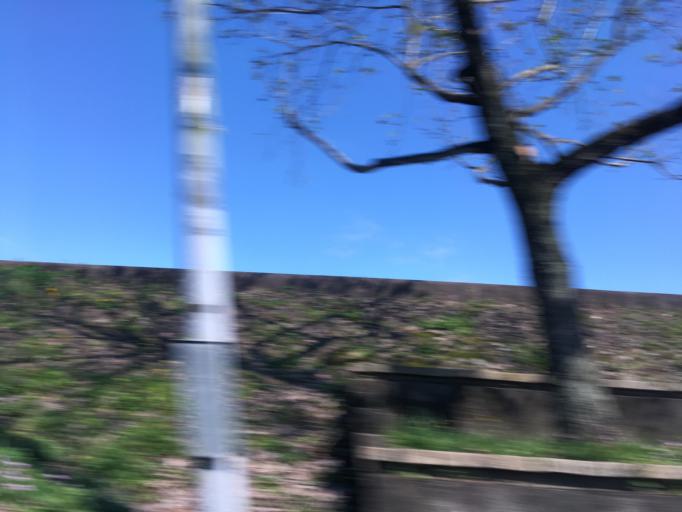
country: TW
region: Taiwan
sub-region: Yilan
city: Yilan
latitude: 24.7571
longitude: 121.7393
